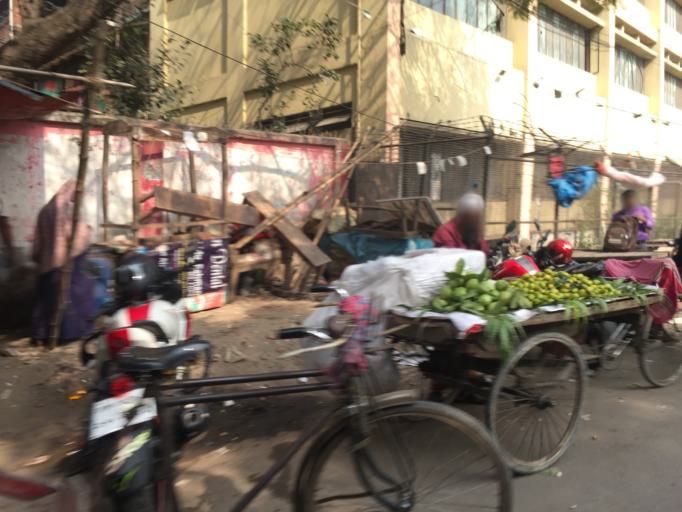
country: BD
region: Dhaka
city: Paltan
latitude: 23.7335
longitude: 90.4085
